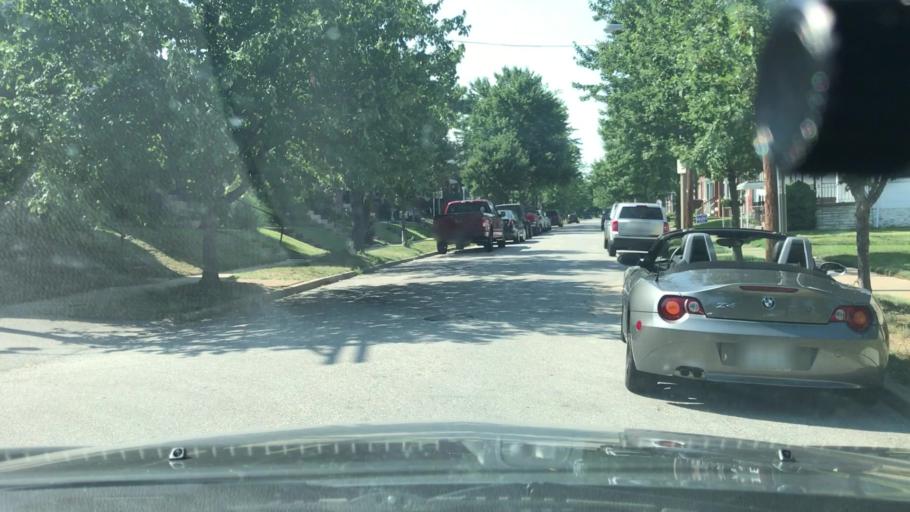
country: US
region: Missouri
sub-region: Saint Louis County
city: Lemay
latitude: 38.5768
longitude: -90.2764
